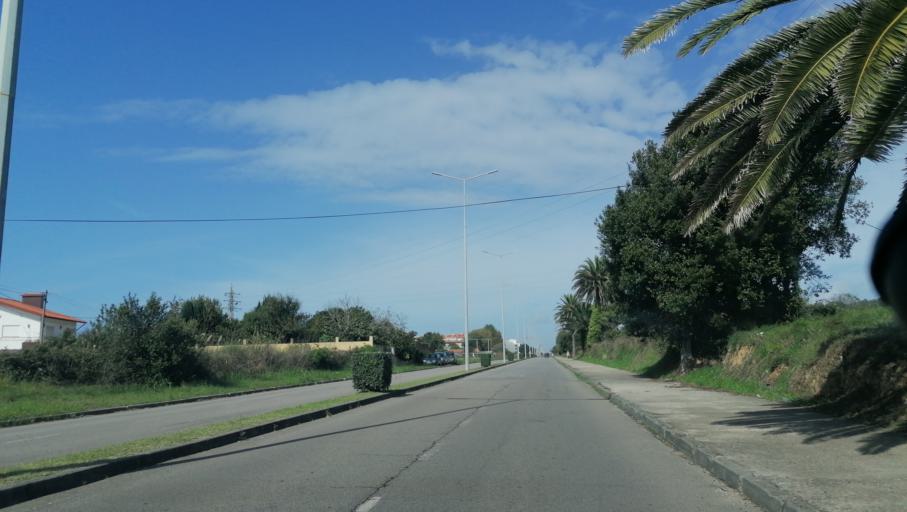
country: PT
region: Aveiro
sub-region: Espinho
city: Silvalde
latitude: 40.9992
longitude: -8.6343
